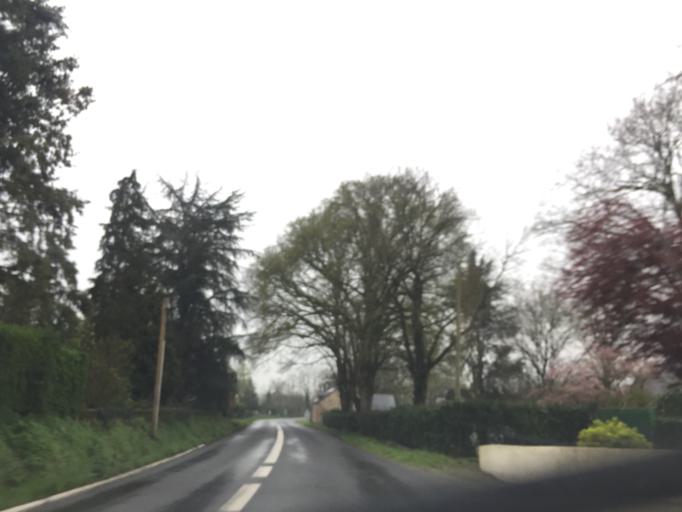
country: FR
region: Pays de la Loire
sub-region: Departement de la Loire-Atlantique
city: Casson
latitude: 47.4119
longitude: -1.5338
